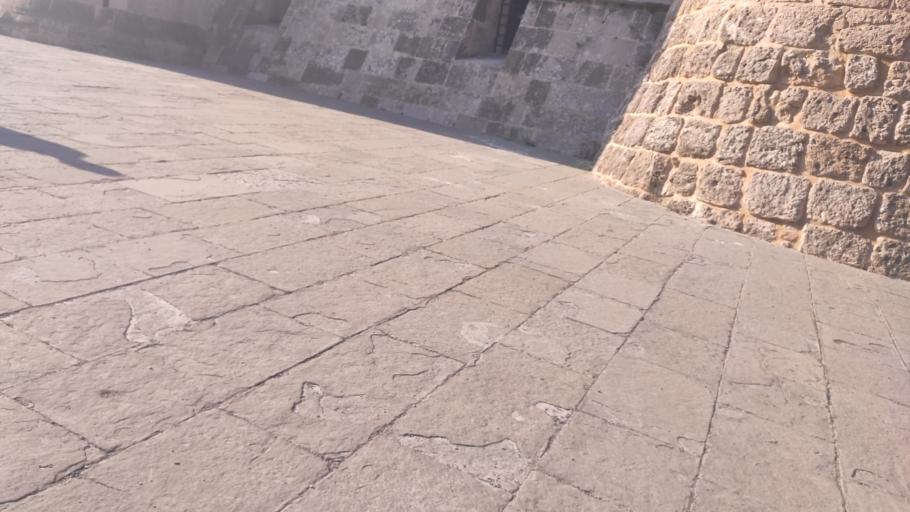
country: GR
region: South Aegean
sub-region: Nomos Dodekanisou
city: Rodos
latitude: 36.4453
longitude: 28.2244
